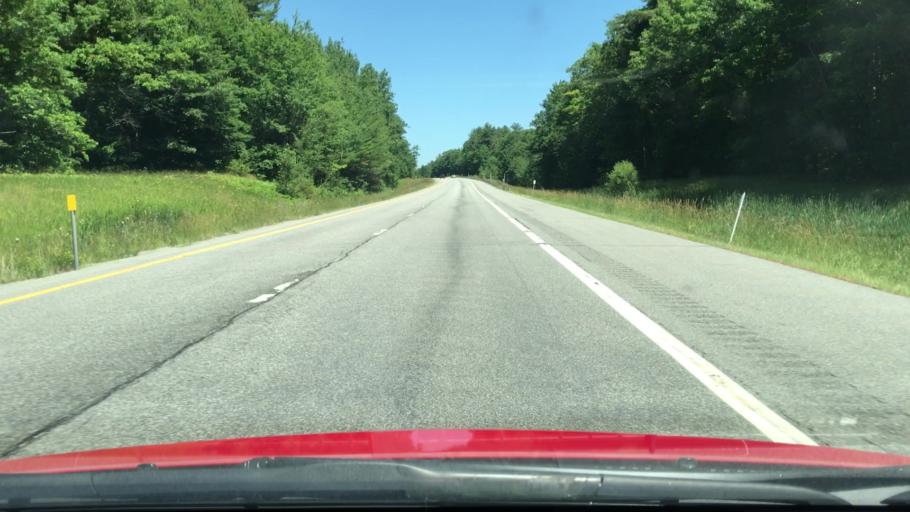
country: US
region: New York
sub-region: Essex County
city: Mineville
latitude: 44.1316
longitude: -73.5884
